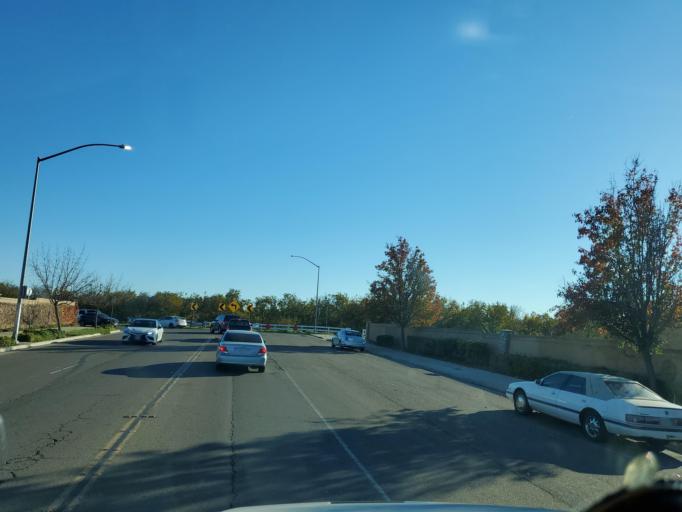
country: US
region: California
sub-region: San Joaquin County
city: August
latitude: 38.0008
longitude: -121.2705
